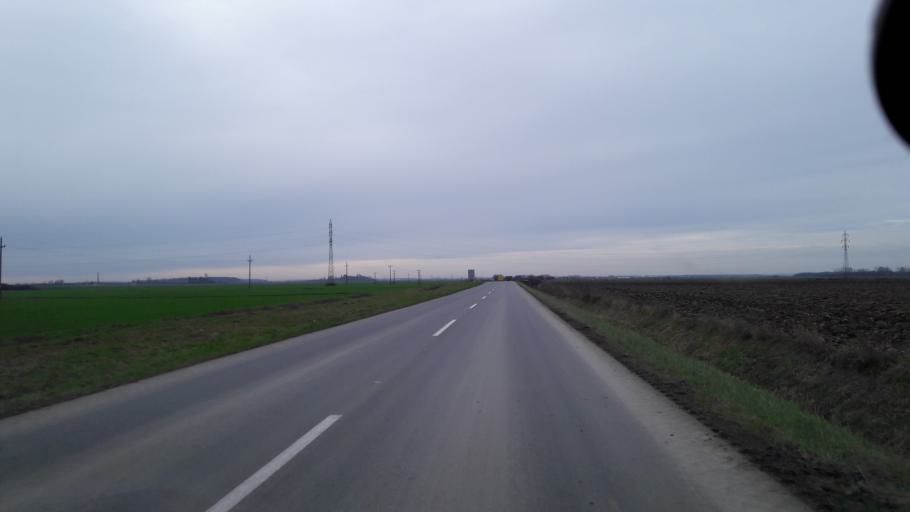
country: HR
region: Osjecko-Baranjska
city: Ovcara
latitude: 45.5007
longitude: 18.5586
